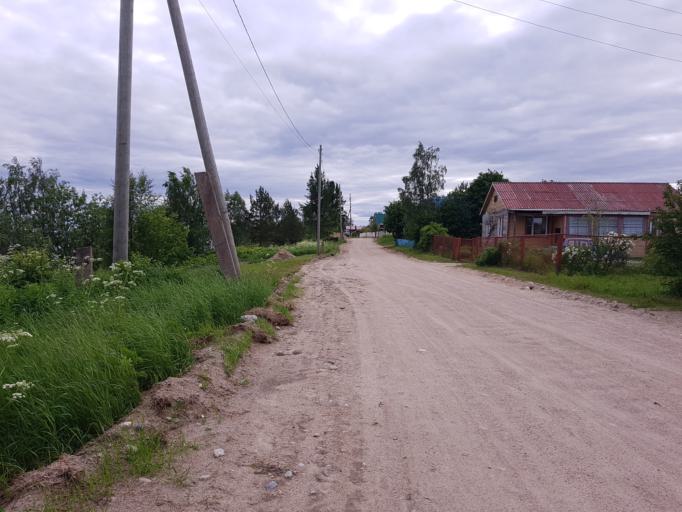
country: RU
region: Republic of Karelia
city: Kalevala
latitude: 65.1909
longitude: 31.1628
